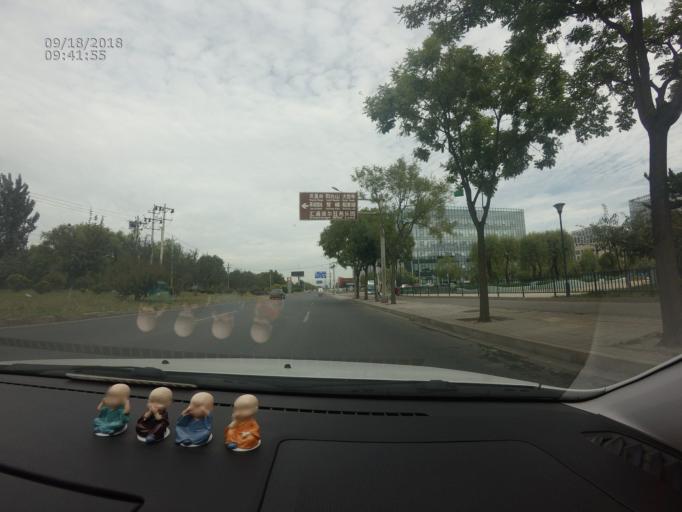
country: CN
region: Beijing
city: Xibeiwang
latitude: 40.0696
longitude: 116.2397
